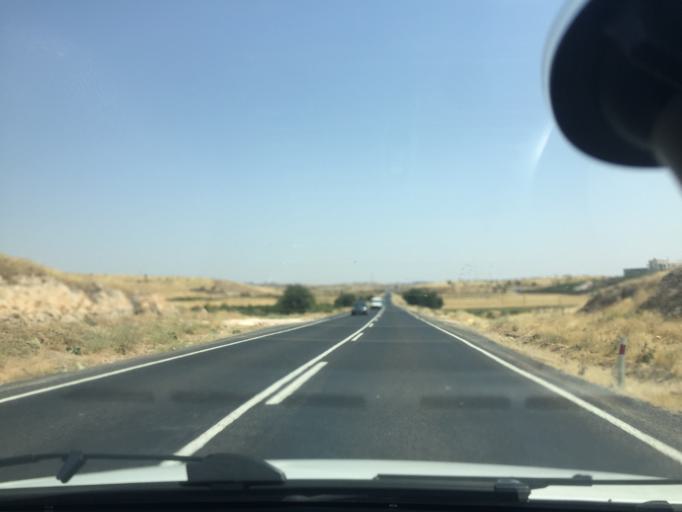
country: TR
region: Mardin
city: Kindirip
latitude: 37.4546
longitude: 41.2498
